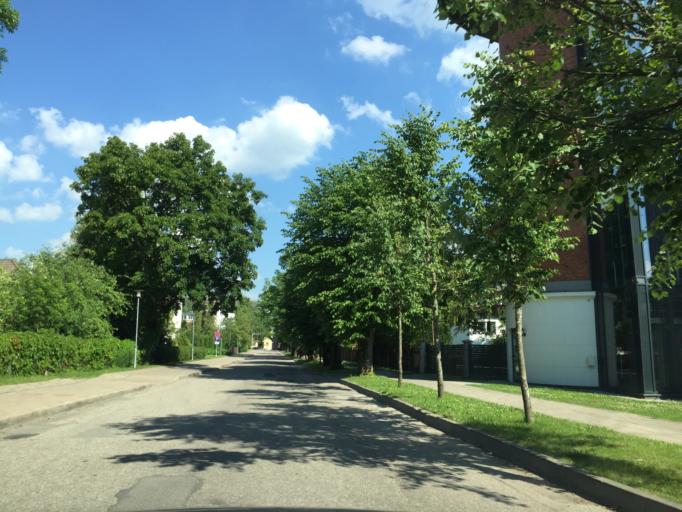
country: LV
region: Sigulda
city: Sigulda
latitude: 57.1568
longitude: 24.8466
